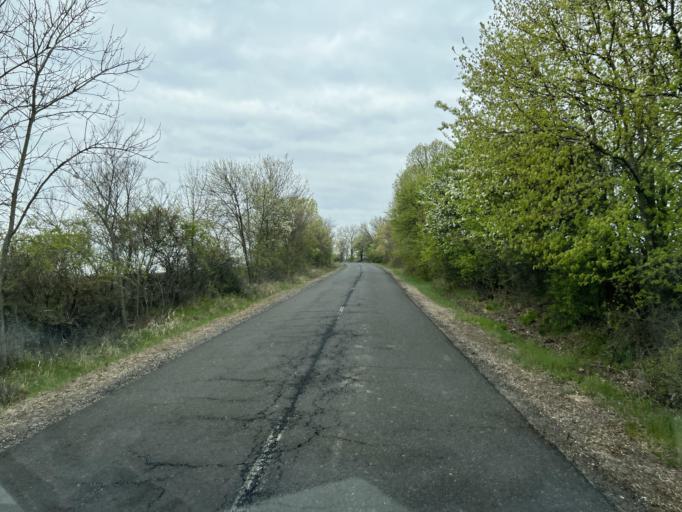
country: HU
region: Pest
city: Acsa
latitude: 47.7881
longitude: 19.4153
